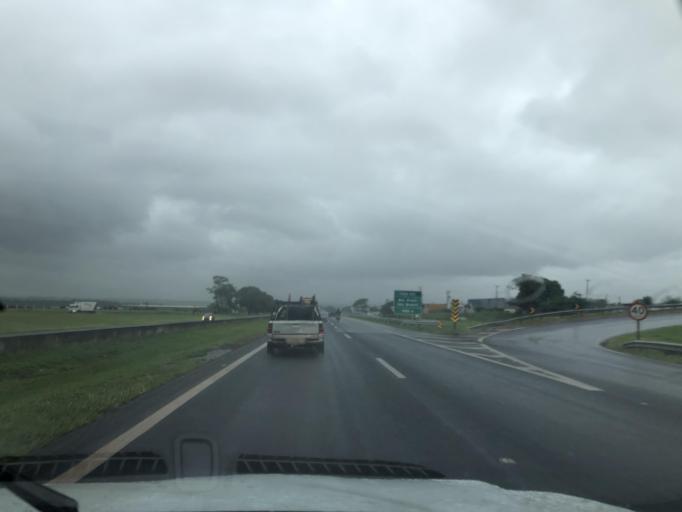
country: BR
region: Sao Paulo
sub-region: Ribeirao Preto
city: Ribeirao Preto
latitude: -21.1139
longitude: -47.7795
